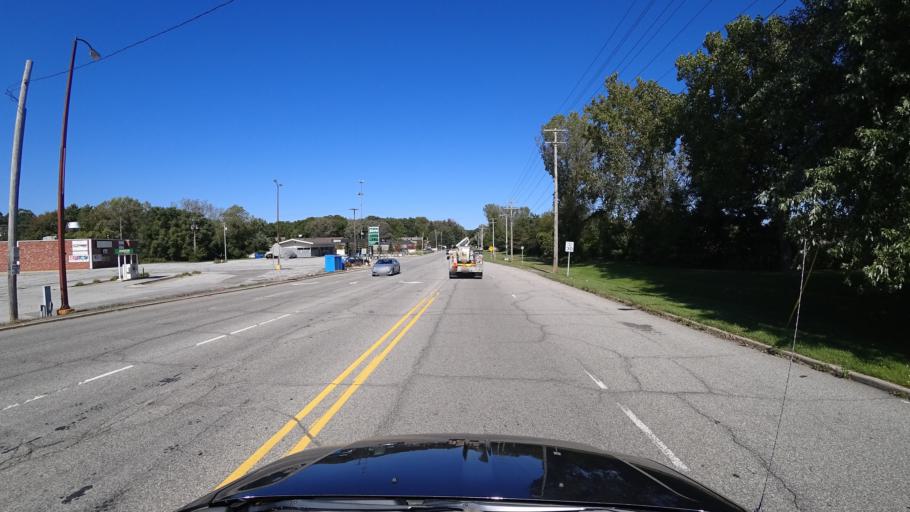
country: US
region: Indiana
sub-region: LaPorte County
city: Long Beach
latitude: 41.7341
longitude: -86.8555
